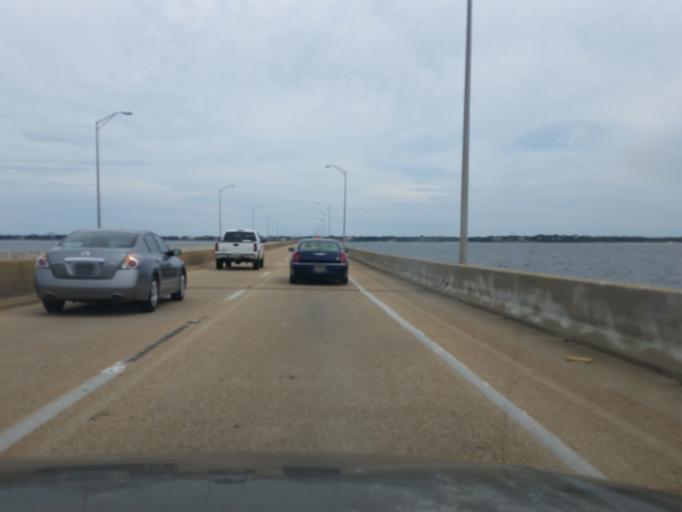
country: US
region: Florida
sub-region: Escambia County
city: East Pensacola Heights
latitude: 30.3906
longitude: -87.1837
